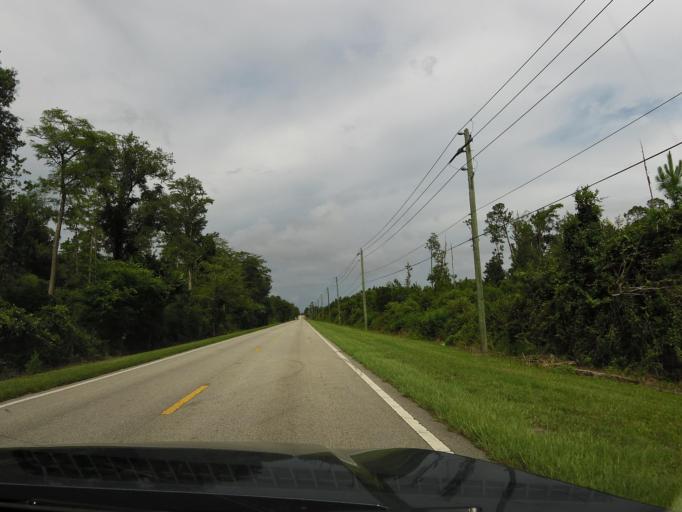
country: US
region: Florida
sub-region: Saint Johns County
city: Saint Augustine South
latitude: 29.8602
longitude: -81.4060
